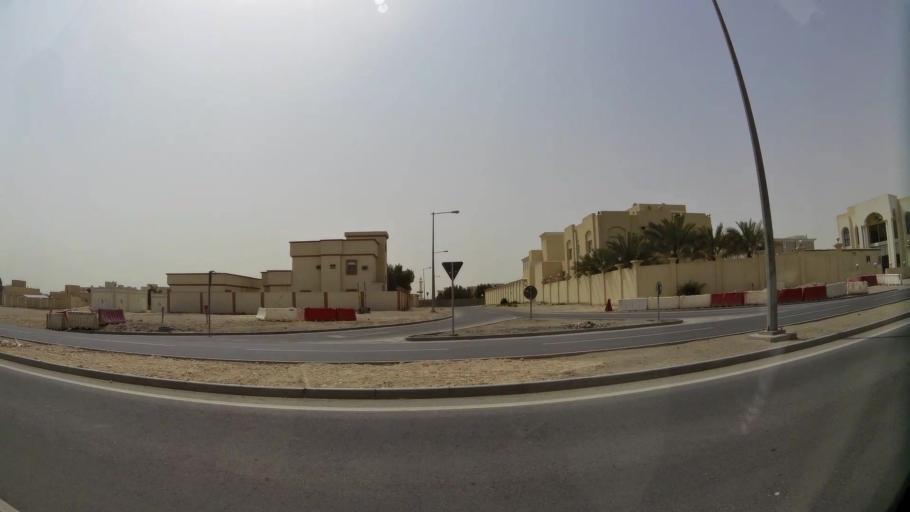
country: QA
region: Baladiyat ar Rayyan
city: Ar Rayyan
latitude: 25.2371
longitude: 51.3820
